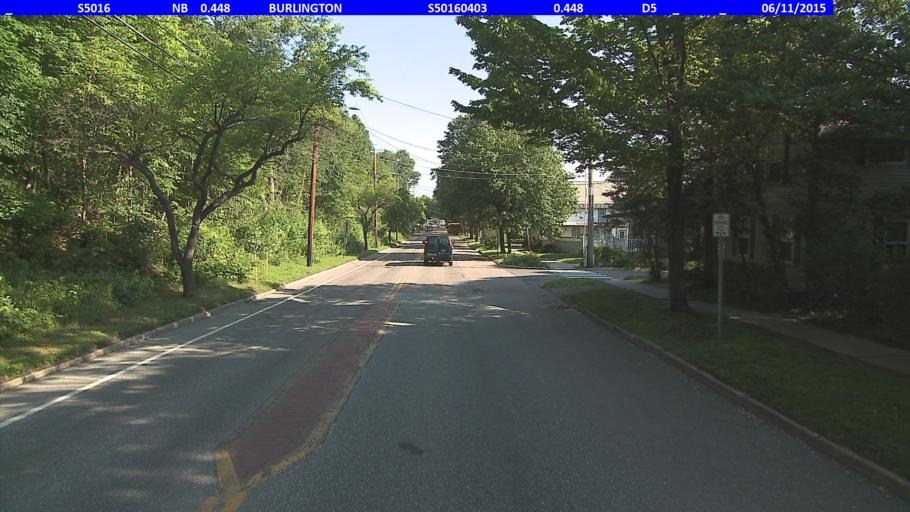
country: US
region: Vermont
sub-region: Chittenden County
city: Winooski
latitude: 44.4790
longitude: -73.1918
